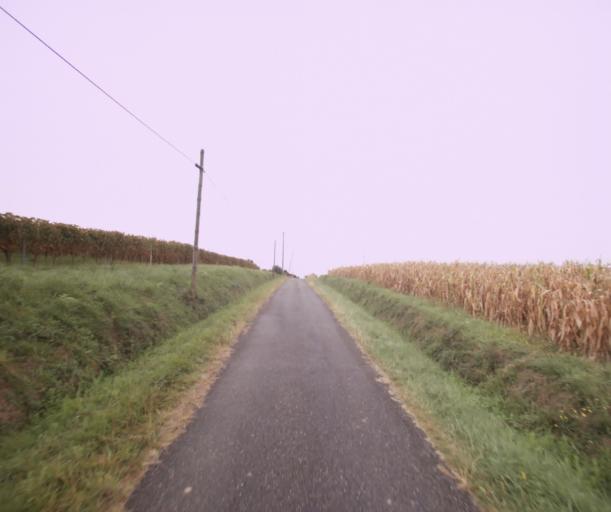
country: FR
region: Midi-Pyrenees
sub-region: Departement du Gers
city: Cazaubon
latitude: 43.8784
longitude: -0.0920
